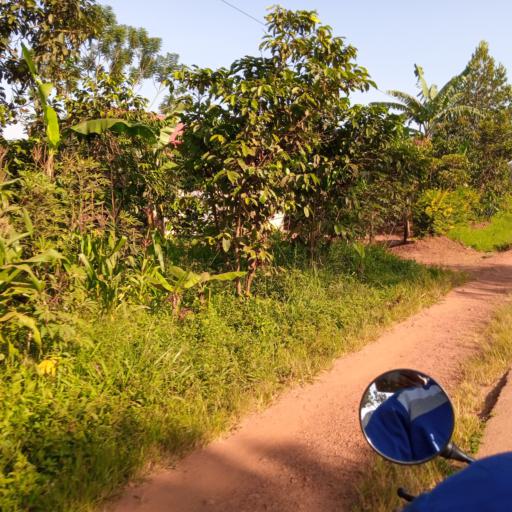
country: UG
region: Central Region
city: Masaka
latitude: -0.4437
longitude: 31.6661
